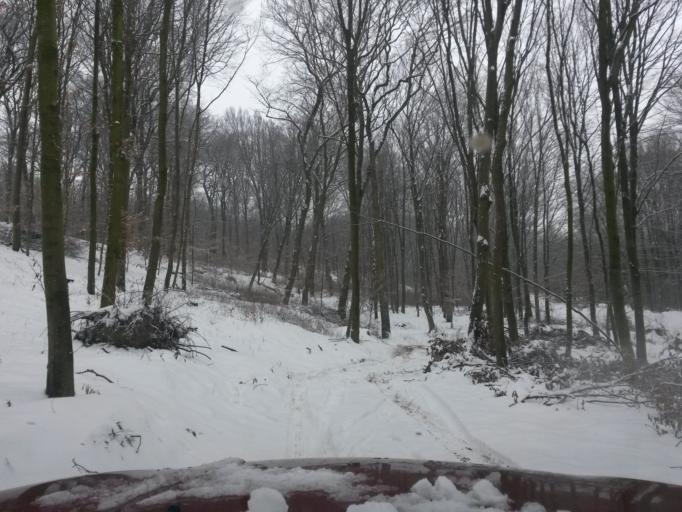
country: SK
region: Kosicky
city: Kosice
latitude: 48.7175
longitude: 21.3269
